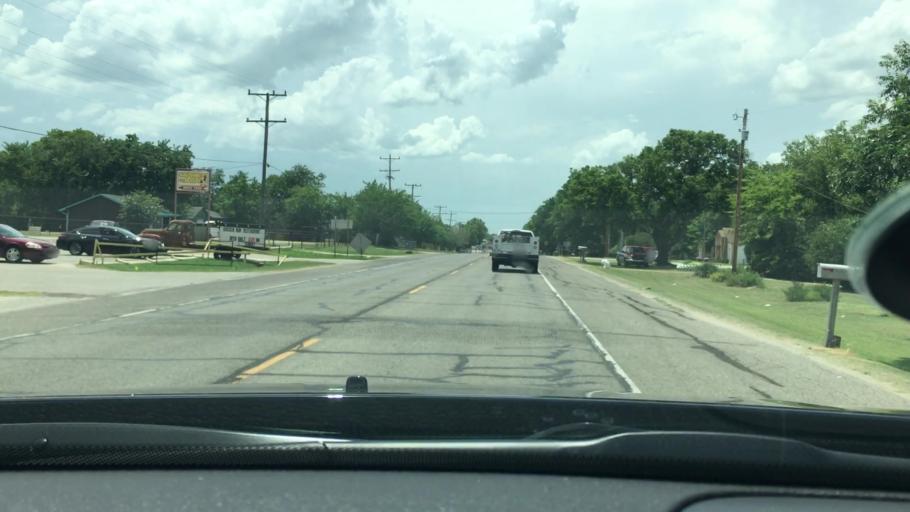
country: US
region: Oklahoma
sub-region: Love County
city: Marietta
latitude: 33.9460
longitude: -97.1263
